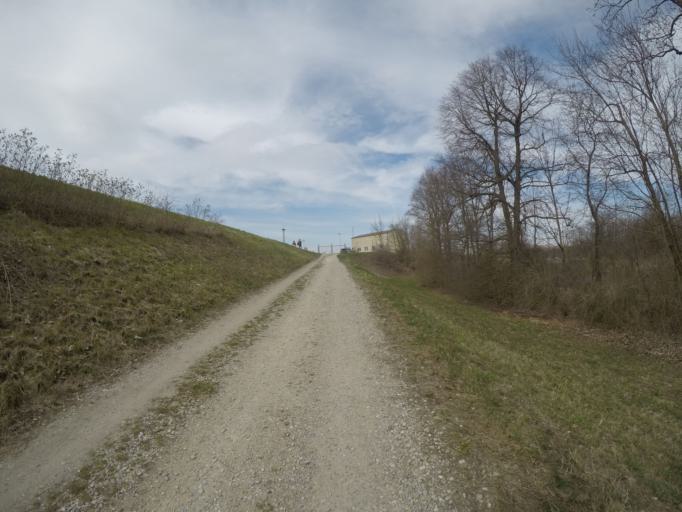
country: DE
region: Bavaria
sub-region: Lower Bavaria
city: Stallwang
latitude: 48.5811
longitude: 12.2194
